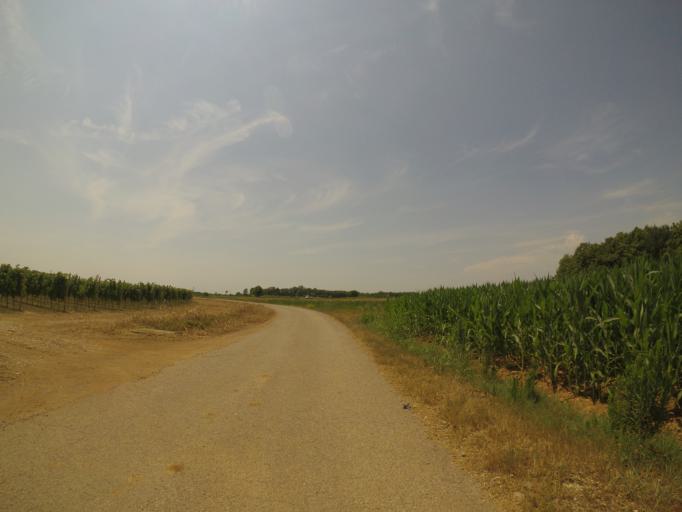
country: IT
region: Friuli Venezia Giulia
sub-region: Provincia di Udine
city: Bertiolo
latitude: 45.9533
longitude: 13.0379
